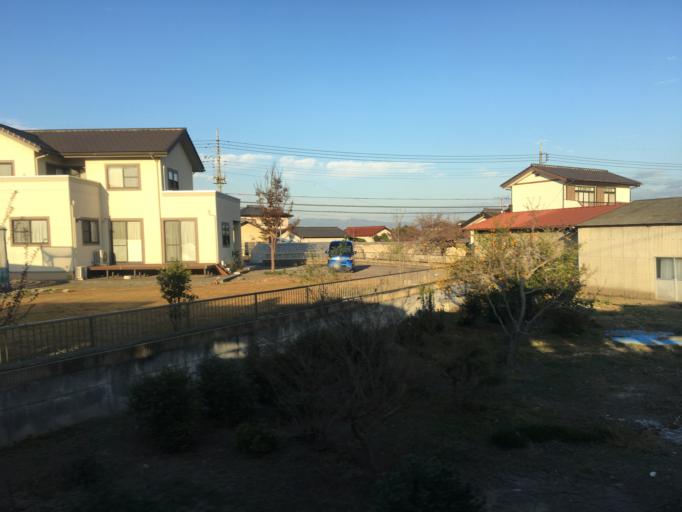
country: JP
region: Gunma
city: Isesaki
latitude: 36.3399
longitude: 139.1683
